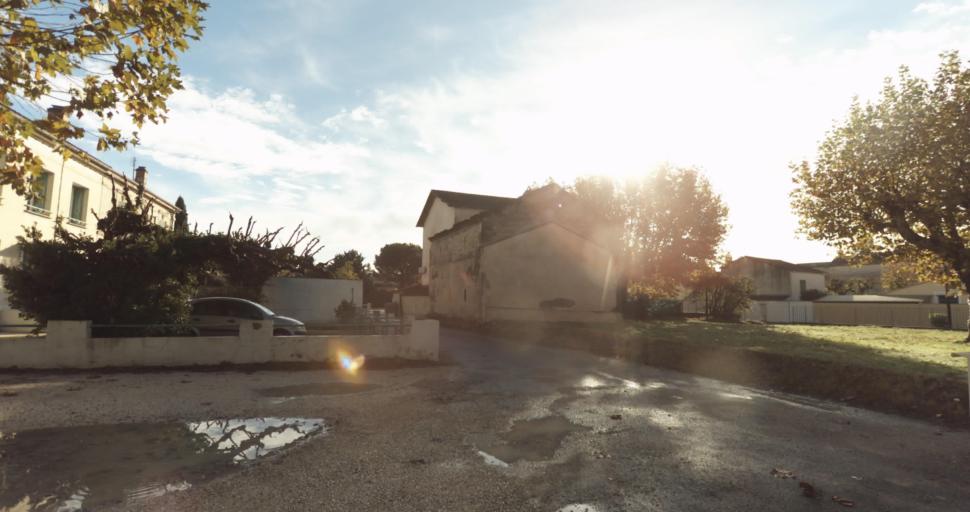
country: FR
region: Provence-Alpes-Cote d'Azur
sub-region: Departement des Bouches-du-Rhone
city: Rognonas
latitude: 43.9013
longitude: 4.8028
